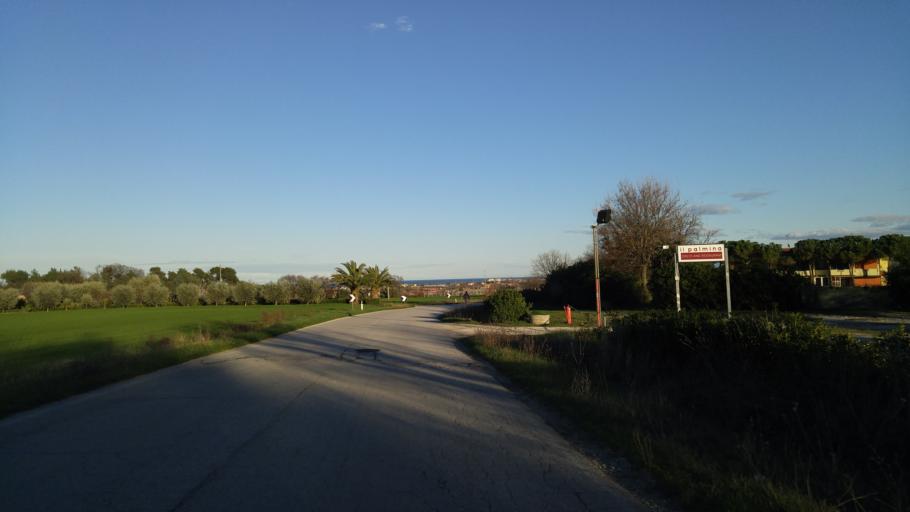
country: IT
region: The Marches
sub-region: Provincia di Pesaro e Urbino
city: Marotta
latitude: 43.7556
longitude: 13.1262
